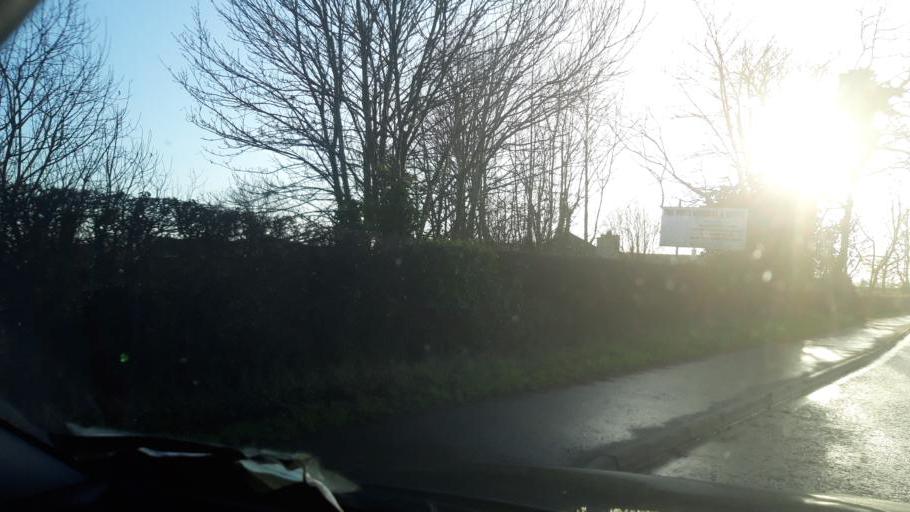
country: GB
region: Northern Ireland
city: Garvagh
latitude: 54.9906
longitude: -6.6841
